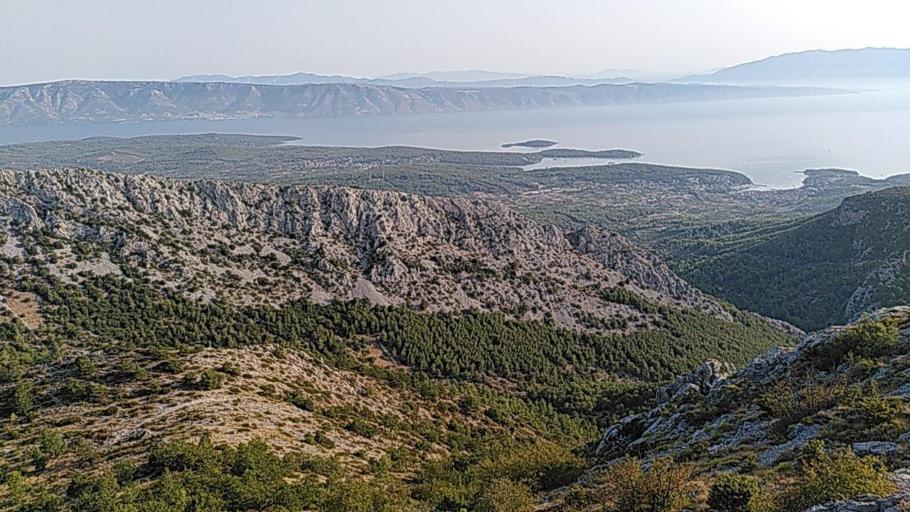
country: HR
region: Splitsko-Dalmatinska
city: Jelsa
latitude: 43.1348
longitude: 16.6637
